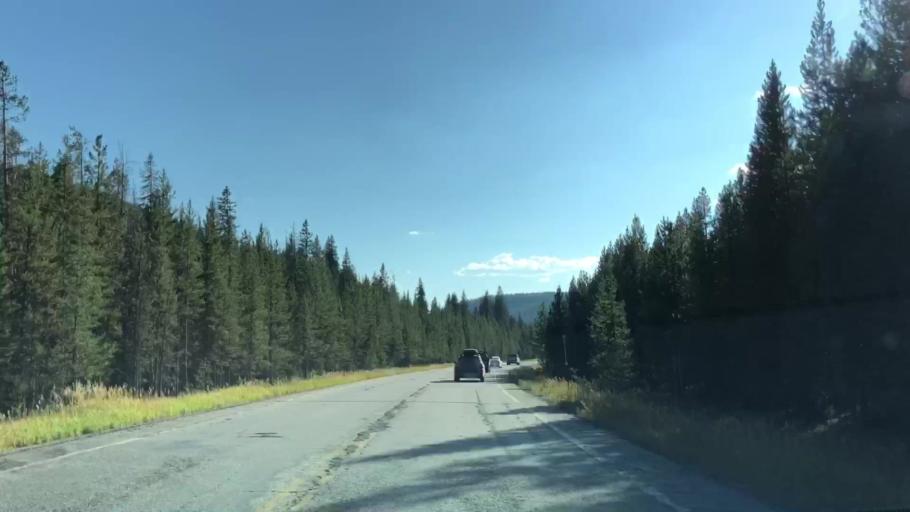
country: US
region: Montana
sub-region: Gallatin County
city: West Yellowstone
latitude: 44.8299
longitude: -111.0789
